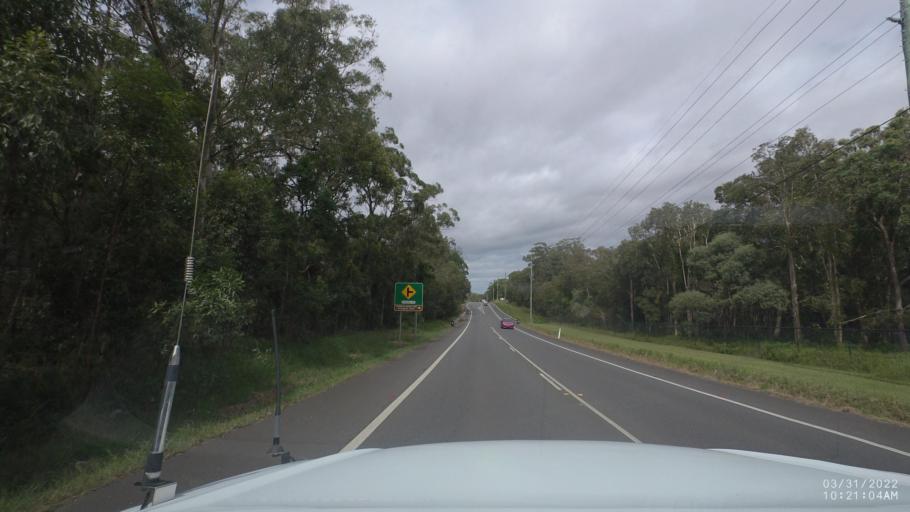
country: AU
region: Queensland
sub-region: Gold Coast
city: Yatala
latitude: -27.6561
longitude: 153.2361
